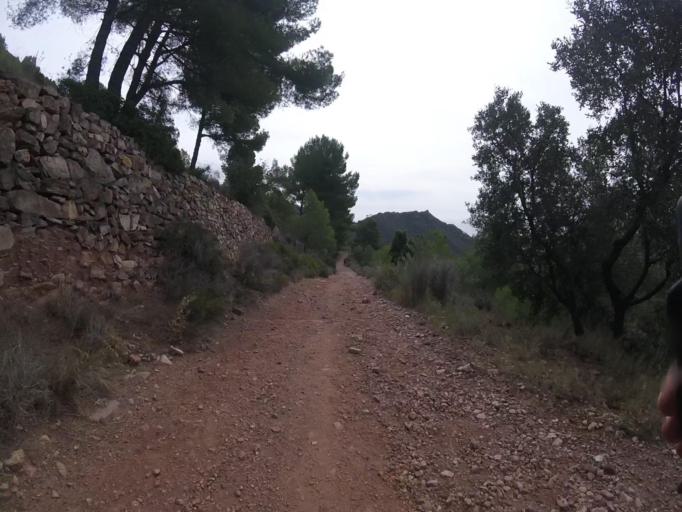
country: ES
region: Valencia
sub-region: Provincia de Castello
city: Benicassim
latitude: 40.0776
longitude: 0.0341
